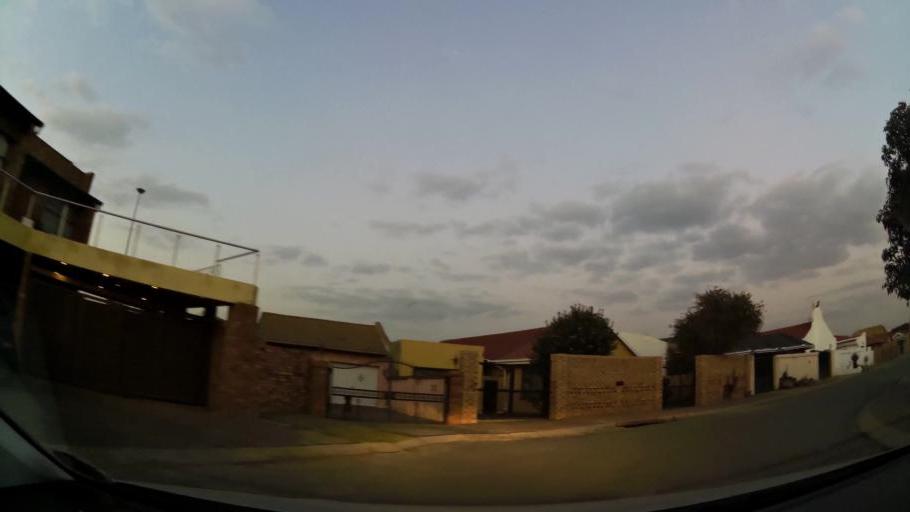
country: ZA
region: Gauteng
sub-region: City of Johannesburg Metropolitan Municipality
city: Soweto
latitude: -26.2702
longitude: 27.9047
